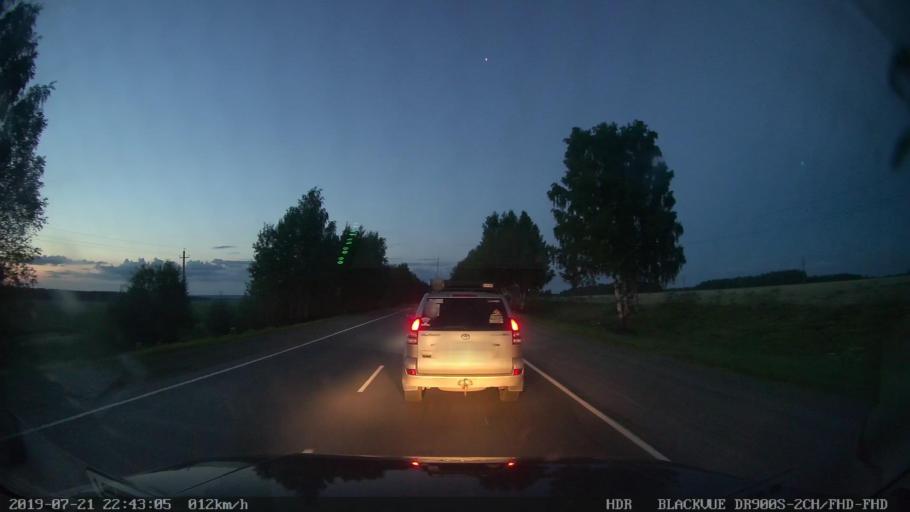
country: RU
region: Perm
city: Ust'-Kachka
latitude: 58.0517
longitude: 55.5953
